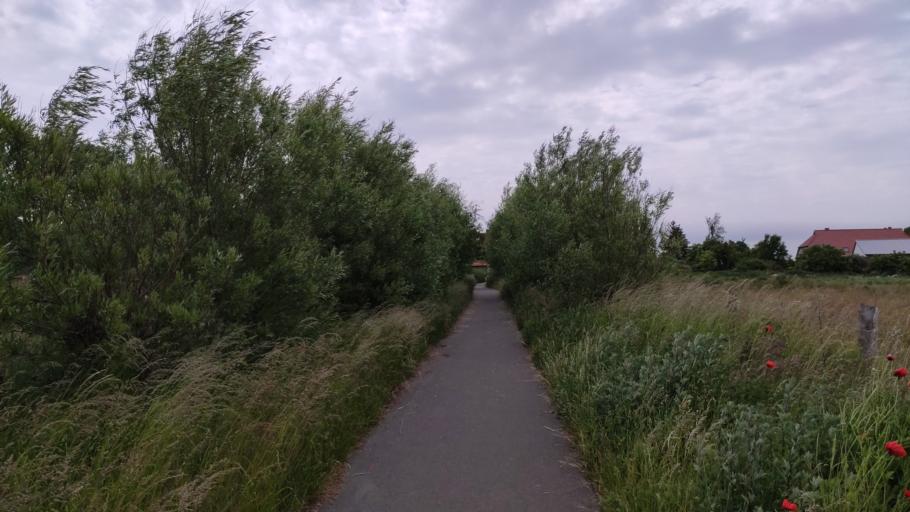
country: DE
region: Mecklenburg-Vorpommern
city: Bastorf
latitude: 54.1374
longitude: 11.6588
